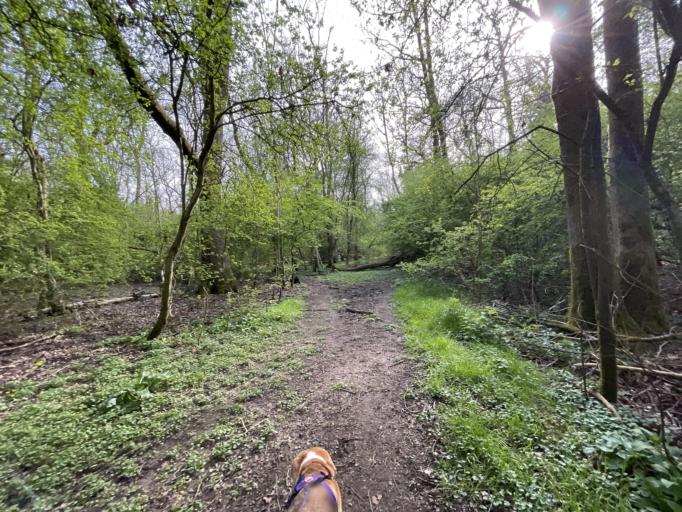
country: GB
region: England
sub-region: Leicestershire
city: Market Harborough
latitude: 52.4231
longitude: -1.0246
